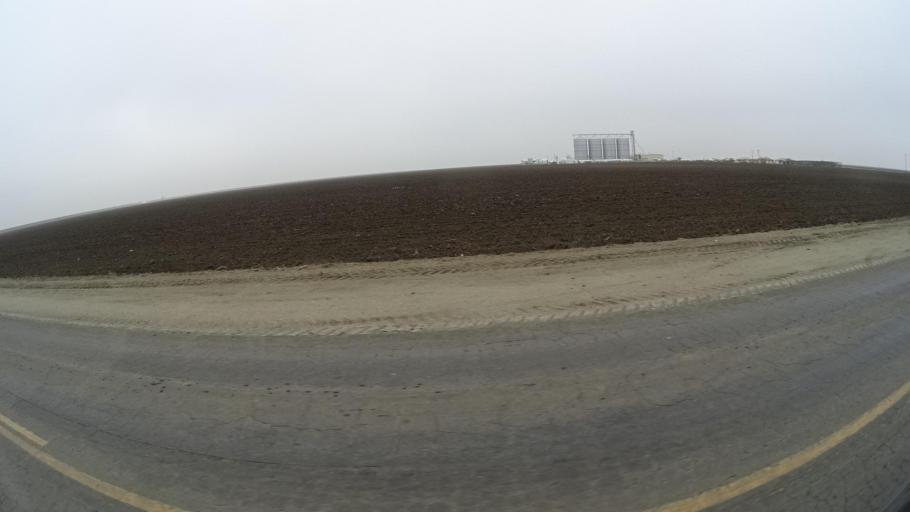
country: US
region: California
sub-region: Kern County
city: Rosedale
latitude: 35.1968
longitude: -119.2329
